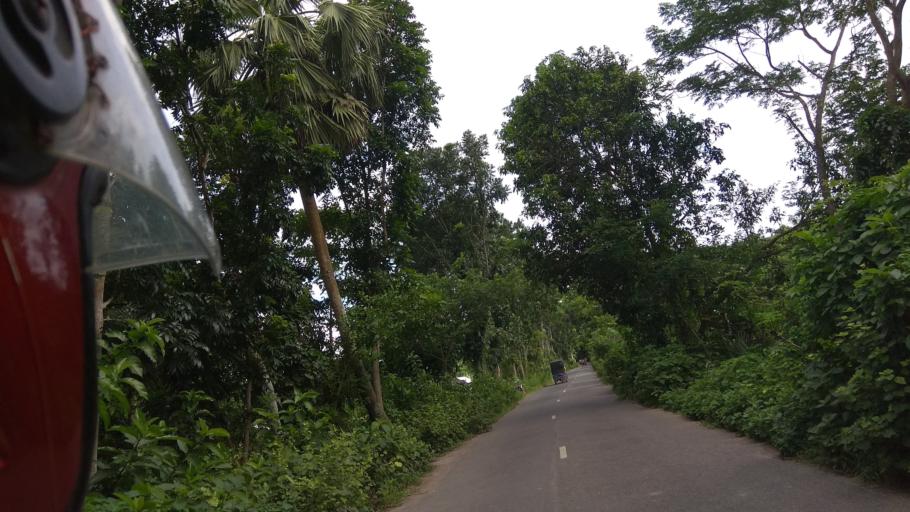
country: BD
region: Khulna
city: Kalia
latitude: 23.1496
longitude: 89.6450
